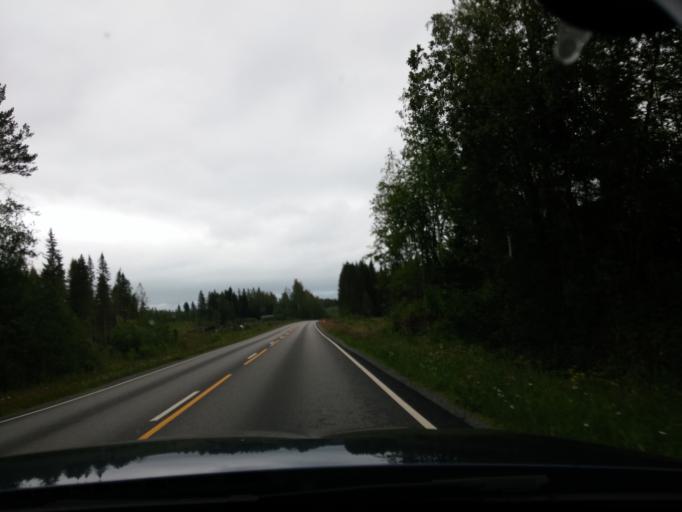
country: FI
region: Central Finland
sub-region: Saarijaervi-Viitasaari
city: Saarijaervi
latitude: 62.6805
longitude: 25.2325
